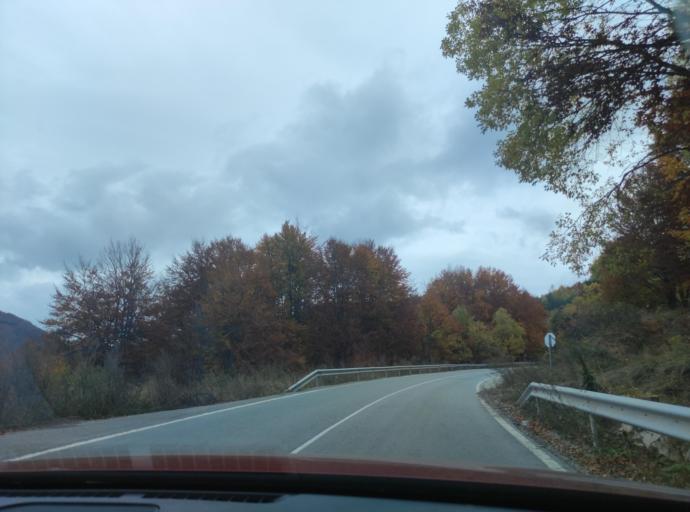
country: BG
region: Sofiya
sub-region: Obshtina Godech
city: Godech
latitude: 43.1057
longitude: 23.1083
